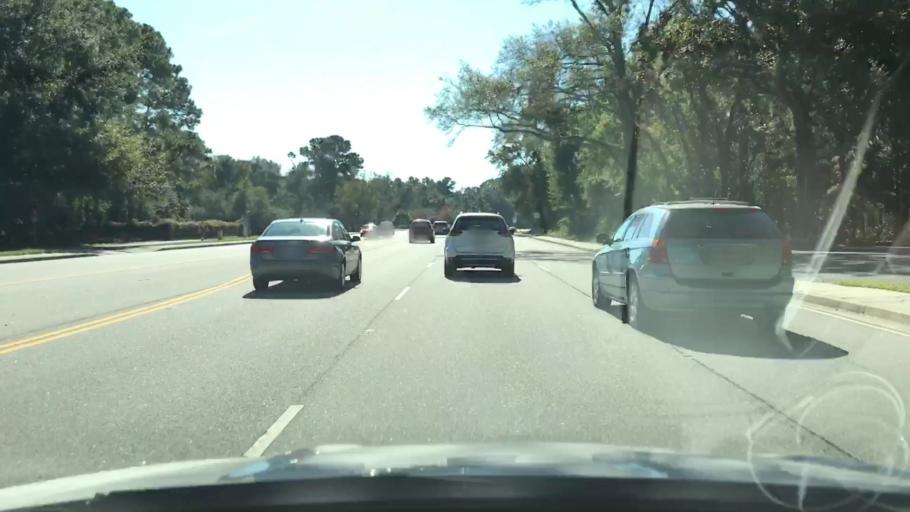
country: US
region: South Carolina
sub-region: Beaufort County
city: Hilton Head Island
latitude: 32.2011
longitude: -80.6994
